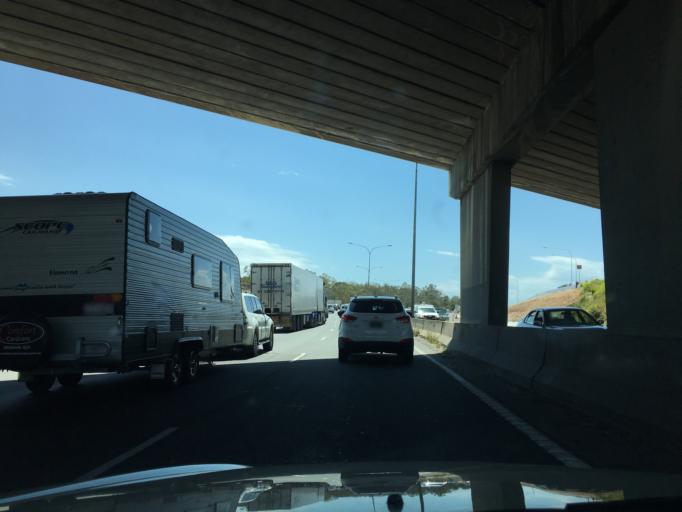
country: AU
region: Queensland
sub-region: Brisbane
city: Shorncliffe
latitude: -27.3741
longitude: 153.0966
